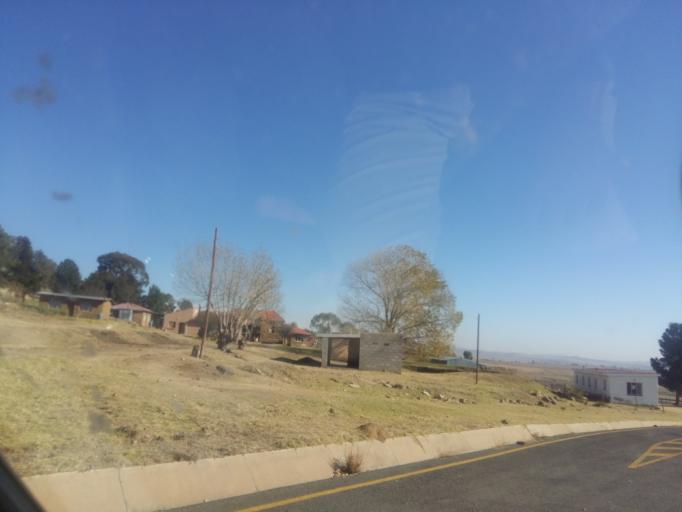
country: LS
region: Mafeteng
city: Mafeteng
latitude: -29.6826
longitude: 27.2820
